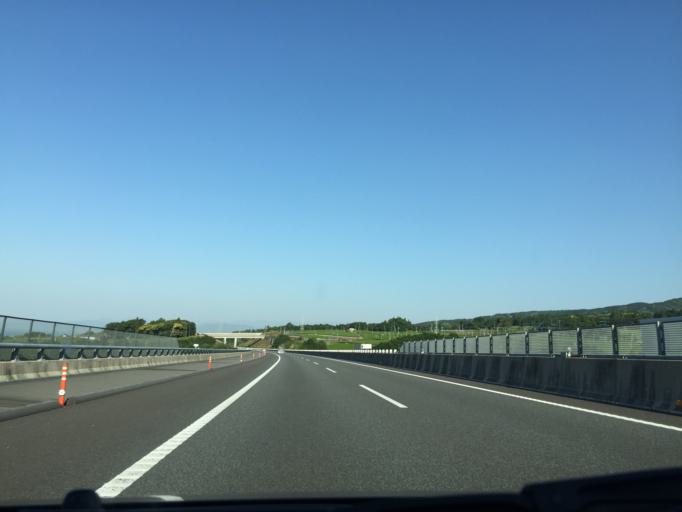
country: JP
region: Shizuoka
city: Numazu
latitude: 35.1547
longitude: 138.8297
